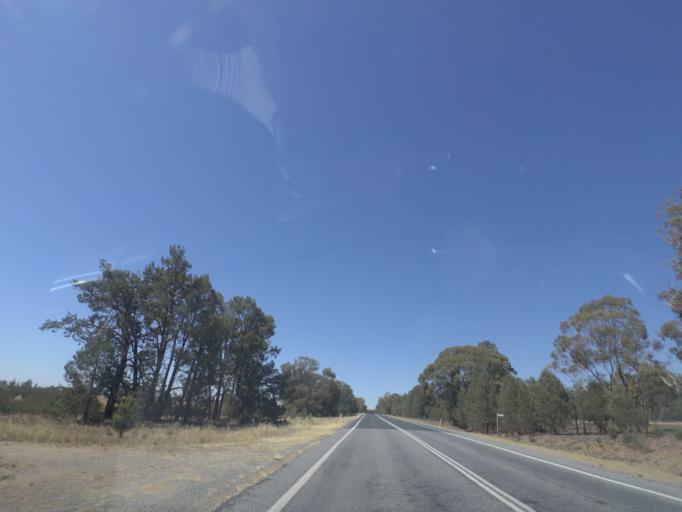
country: AU
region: New South Wales
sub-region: Narrandera
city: Narrandera
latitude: -34.4323
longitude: 146.8430
